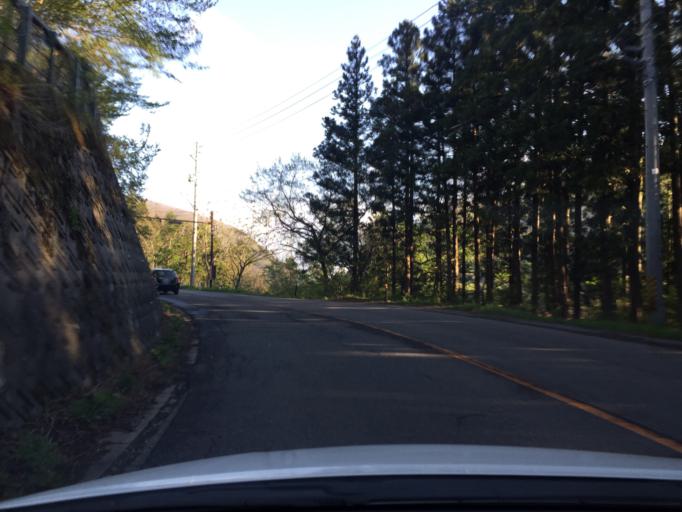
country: JP
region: Fukushima
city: Inawashiro
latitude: 37.6222
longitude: 140.1133
